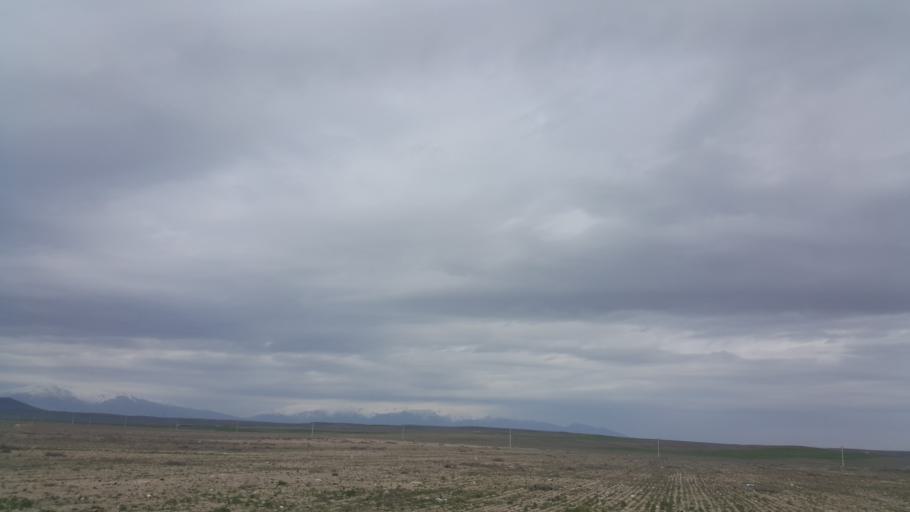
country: TR
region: Nigde
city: Altunhisar
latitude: 37.8513
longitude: 34.1747
